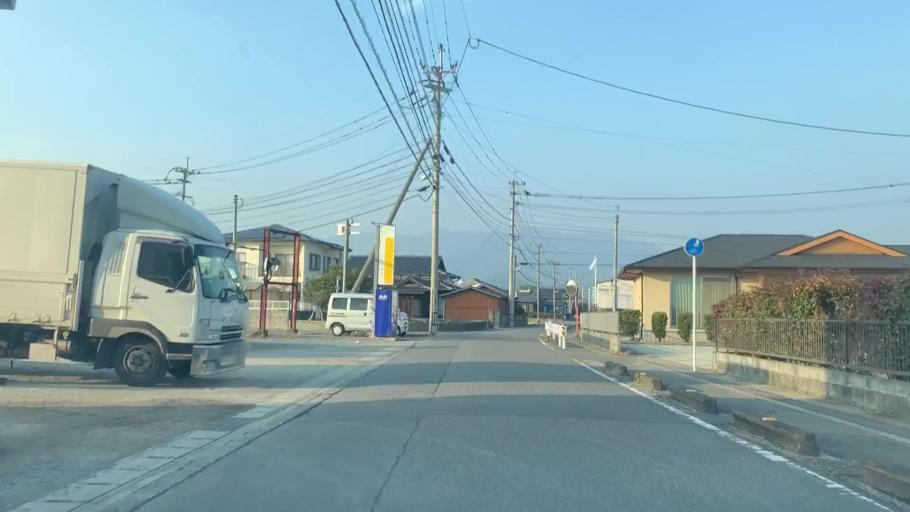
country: JP
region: Saga Prefecture
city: Saga-shi
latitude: 33.2768
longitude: 130.2267
